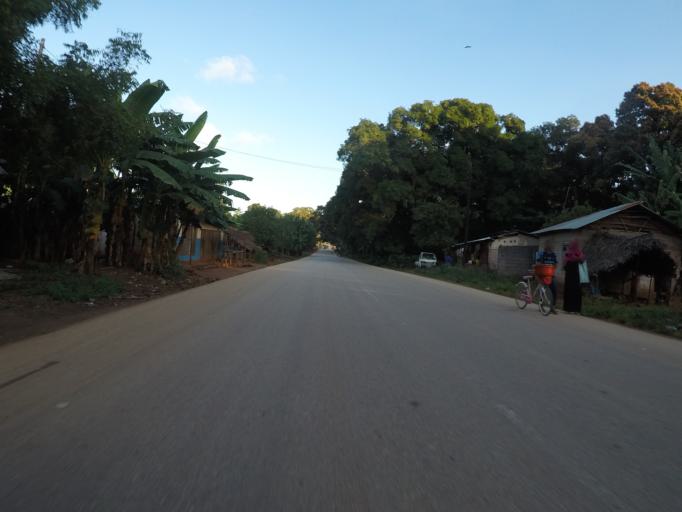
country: TZ
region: Zanzibar North
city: Gamba
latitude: -5.8831
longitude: 39.2843
